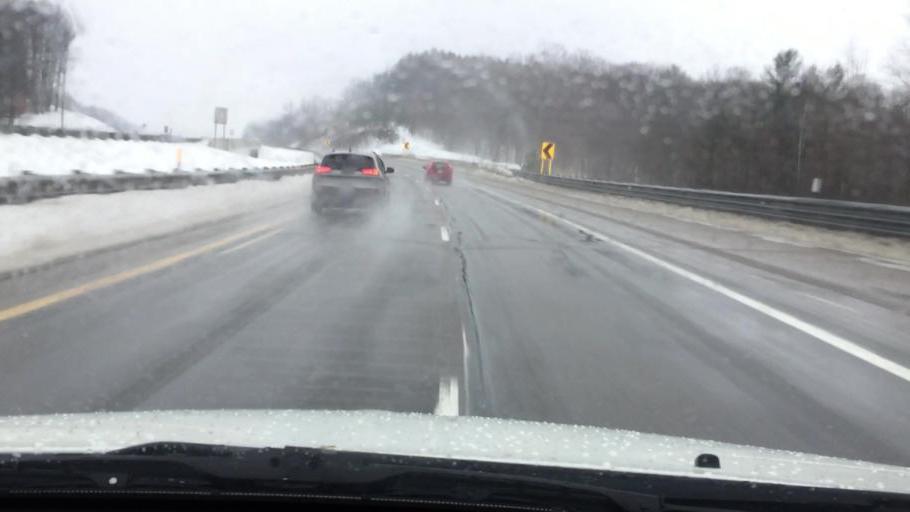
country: US
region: Michigan
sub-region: Wexford County
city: Cadillac
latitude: 44.3003
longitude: -85.3925
